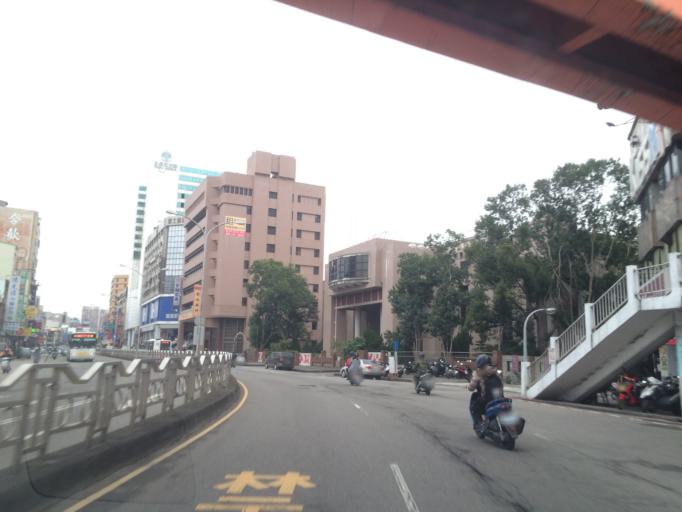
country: TW
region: Taiwan
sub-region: Taichung City
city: Taichung
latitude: 24.1590
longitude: 120.6912
